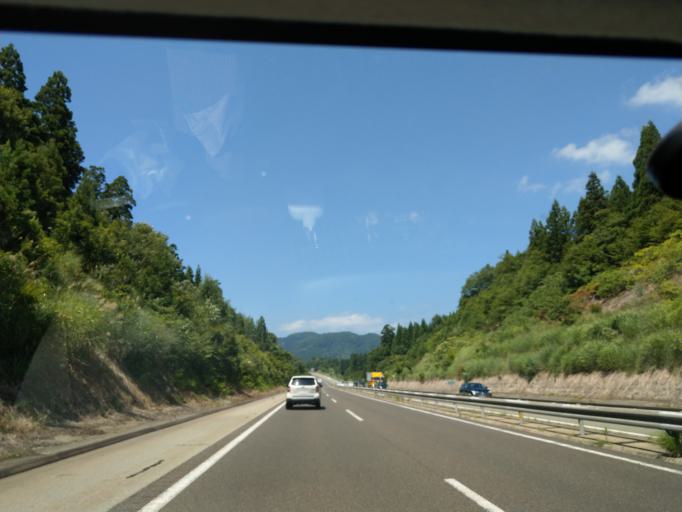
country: JP
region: Akita
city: Omagari
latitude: 39.4157
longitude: 140.4371
